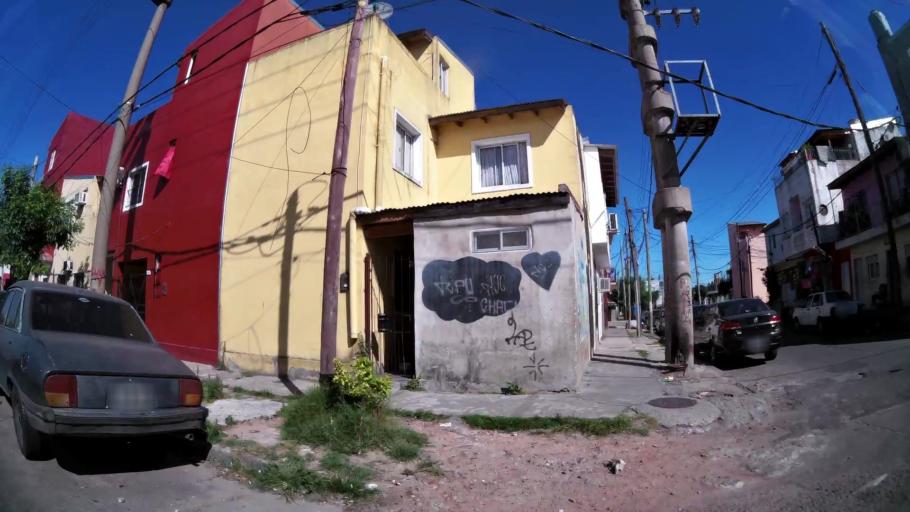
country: AR
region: Buenos Aires
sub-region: Partido de San Isidro
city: San Isidro
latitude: -34.4606
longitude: -58.5437
